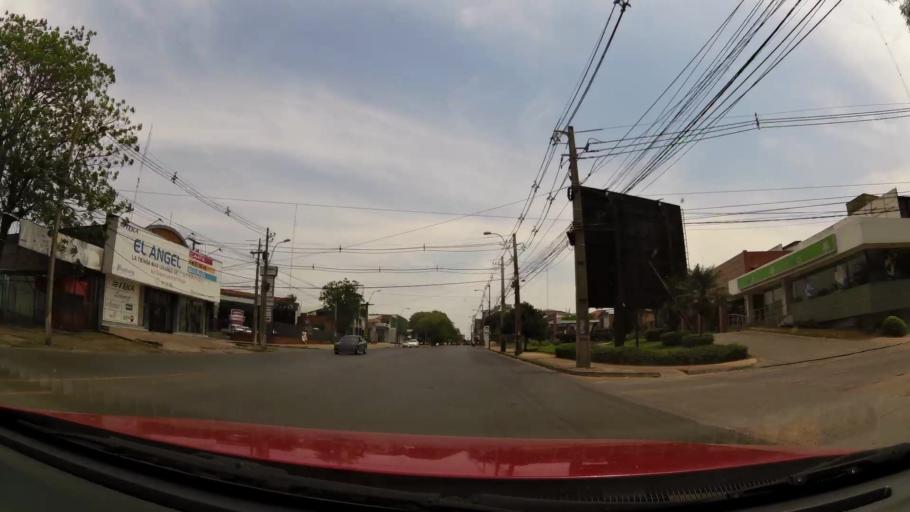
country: PY
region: Central
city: Lambare
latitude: -25.3181
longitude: -57.5680
